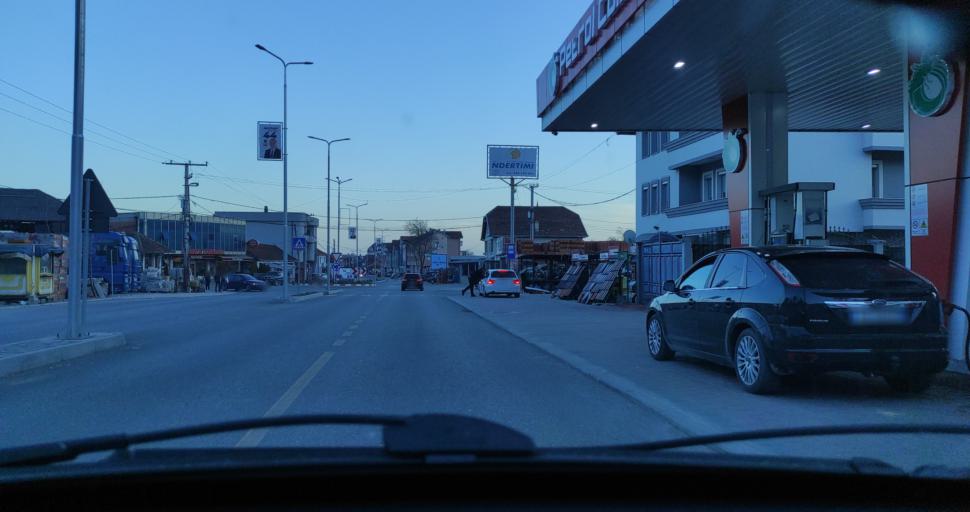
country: XK
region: Gjakova
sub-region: Komuna e Decanit
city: Decan
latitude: 42.5315
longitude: 20.2948
